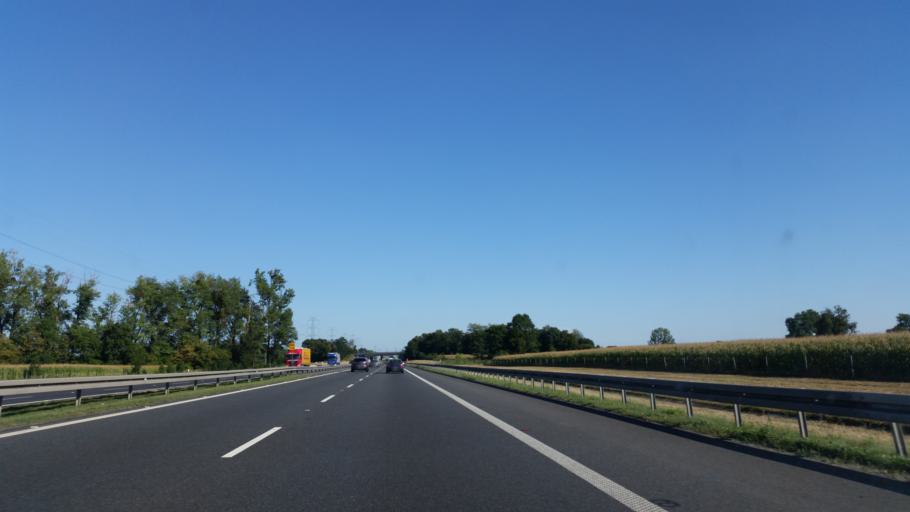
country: PL
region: Lower Silesian Voivodeship
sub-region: Powiat olawski
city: Wierzbno
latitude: 50.9133
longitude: 17.1470
